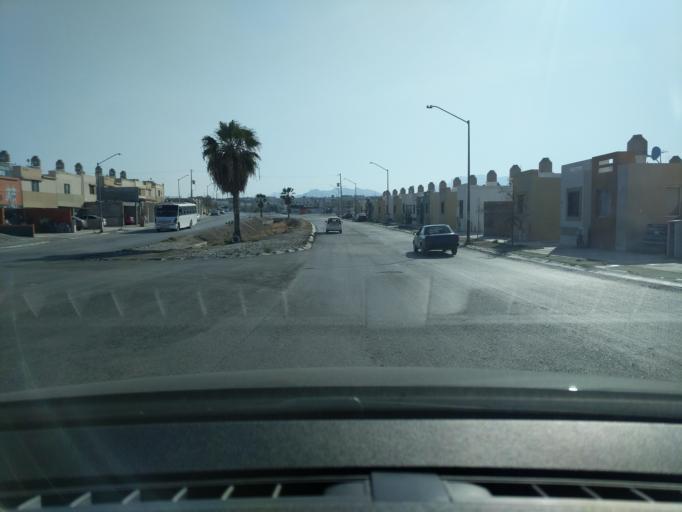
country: MX
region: Coahuila
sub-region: Ramos Arizpe
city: Ramos Arizpe
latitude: 25.5529
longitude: -100.9644
